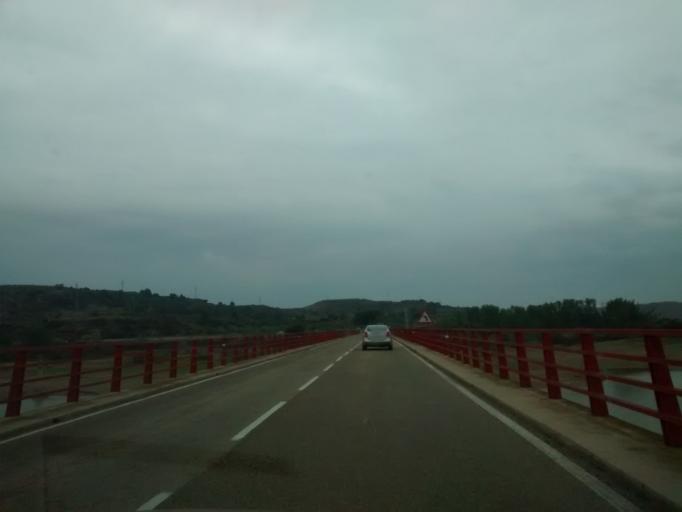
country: ES
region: Aragon
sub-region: Provincia de Zaragoza
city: Caspe
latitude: 41.2600
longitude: -0.0611
